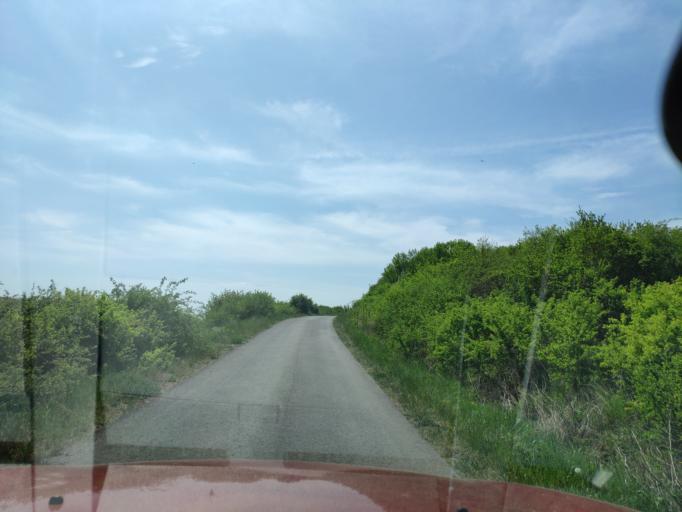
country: SK
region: Banskobystricky
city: Rimavska Sobota
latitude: 48.4215
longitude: 20.1616
